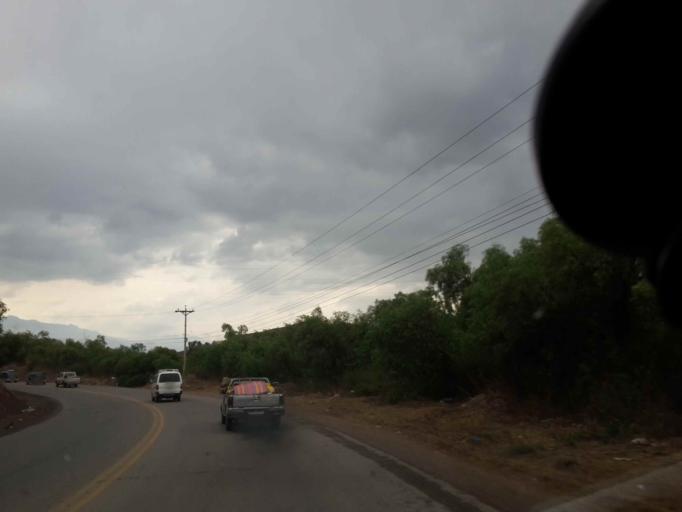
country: BO
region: Cochabamba
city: Sipe Sipe
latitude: -17.5048
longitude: -66.3331
